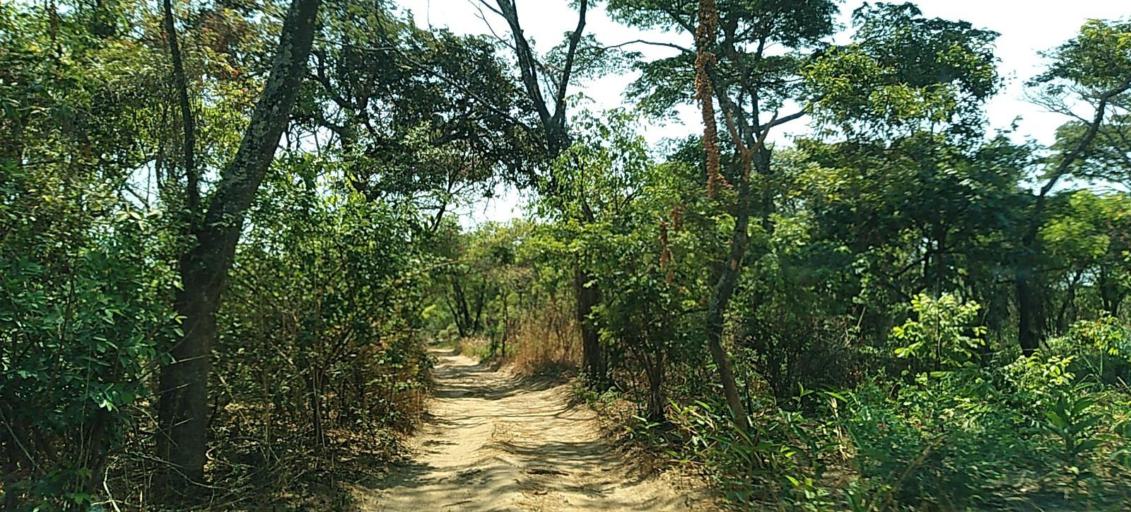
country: ZM
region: North-Western
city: Solwezi
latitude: -12.0981
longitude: 26.2786
